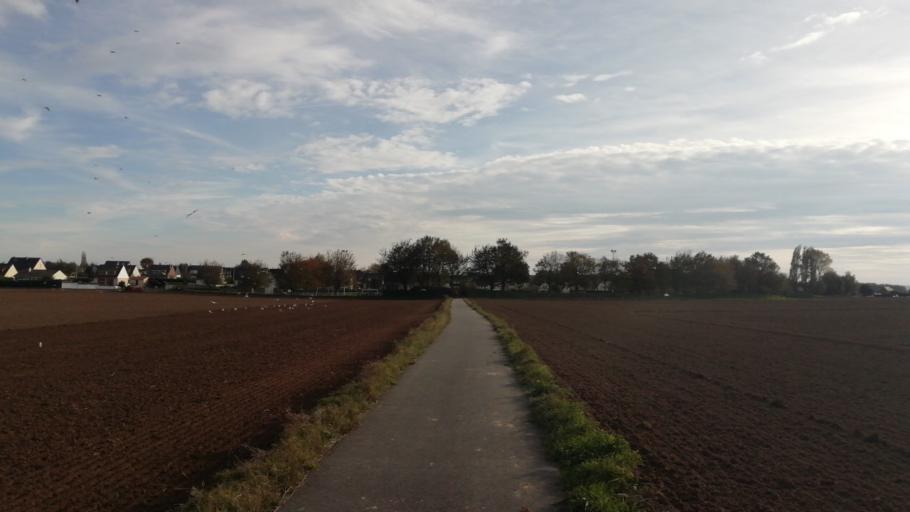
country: FR
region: Haute-Normandie
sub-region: Departement de la Seine-Maritime
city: Rogerville
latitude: 49.5091
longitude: 0.2639
